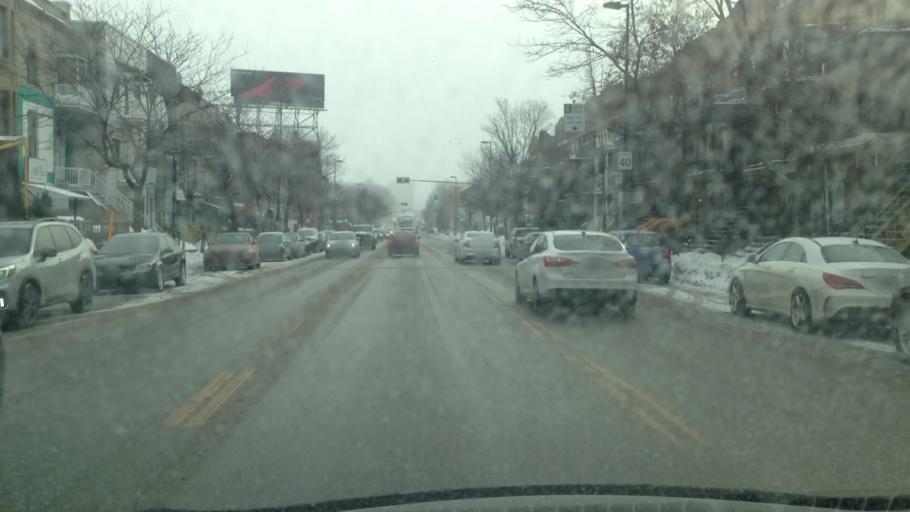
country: CA
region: Quebec
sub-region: Montreal
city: Montreal
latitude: 45.5188
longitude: -73.5940
